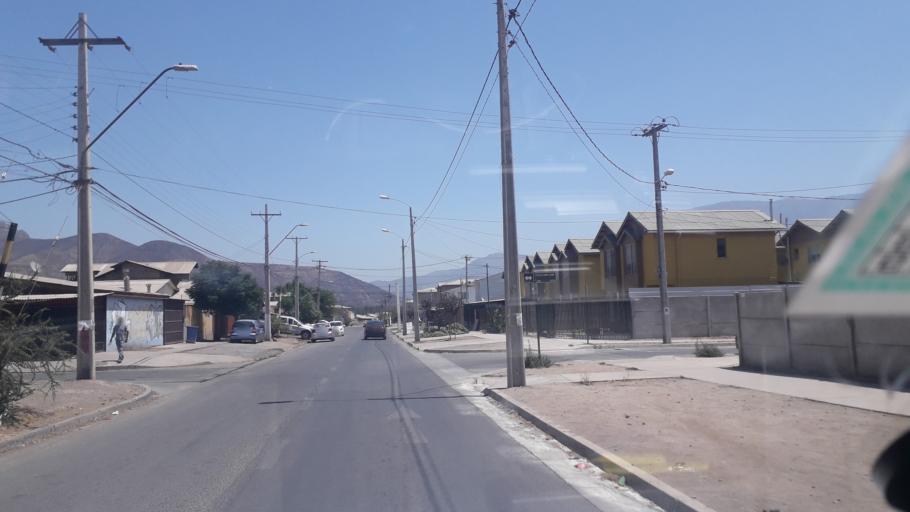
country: CL
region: Valparaiso
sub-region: Provincia de San Felipe
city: San Felipe
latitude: -32.7386
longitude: -70.7362
